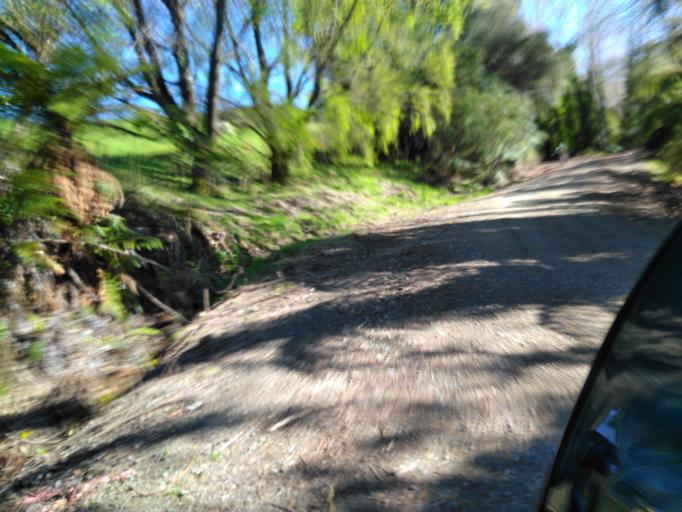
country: NZ
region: Bay of Plenty
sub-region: Opotiki District
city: Opotiki
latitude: -38.3701
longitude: 177.6008
